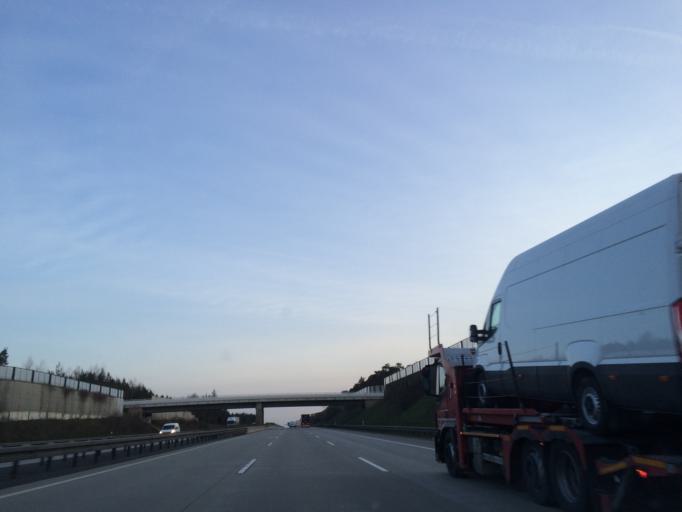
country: DE
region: Thuringia
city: Hermsdorf
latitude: 50.8995
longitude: 11.8435
